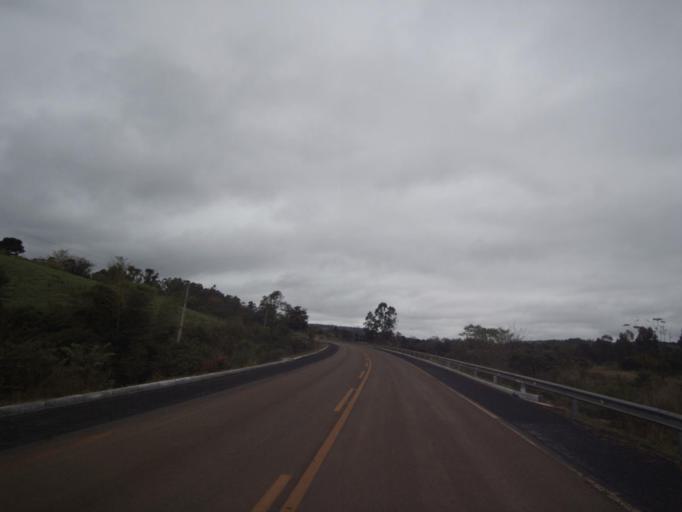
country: AR
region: Misiones
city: El Soberbio
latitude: -27.2918
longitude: -54.1902
